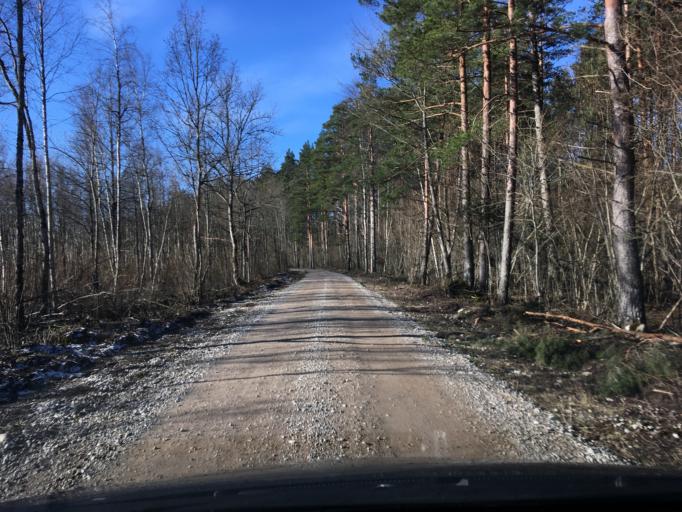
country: EE
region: Laeaene
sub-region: Lihula vald
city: Lihula
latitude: 58.5726
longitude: 23.6961
